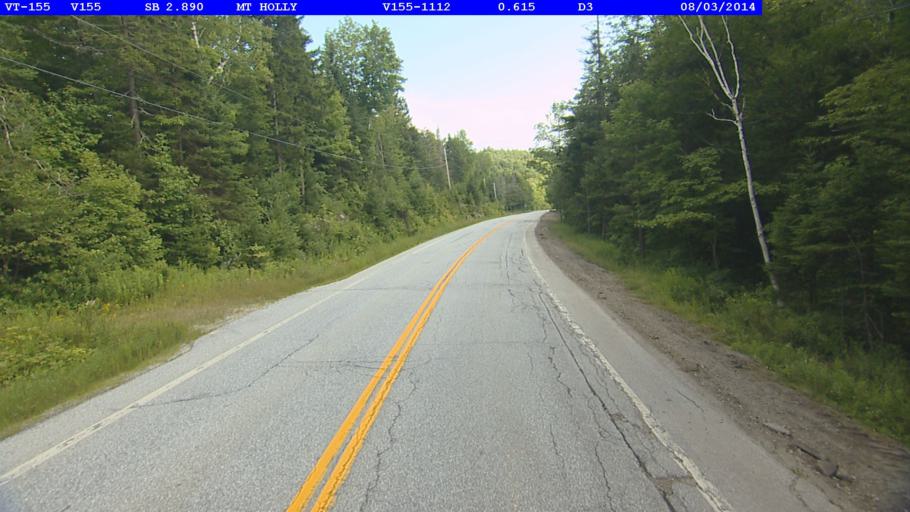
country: US
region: Vermont
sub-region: Windsor County
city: Chester
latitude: 43.3751
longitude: -72.7879
